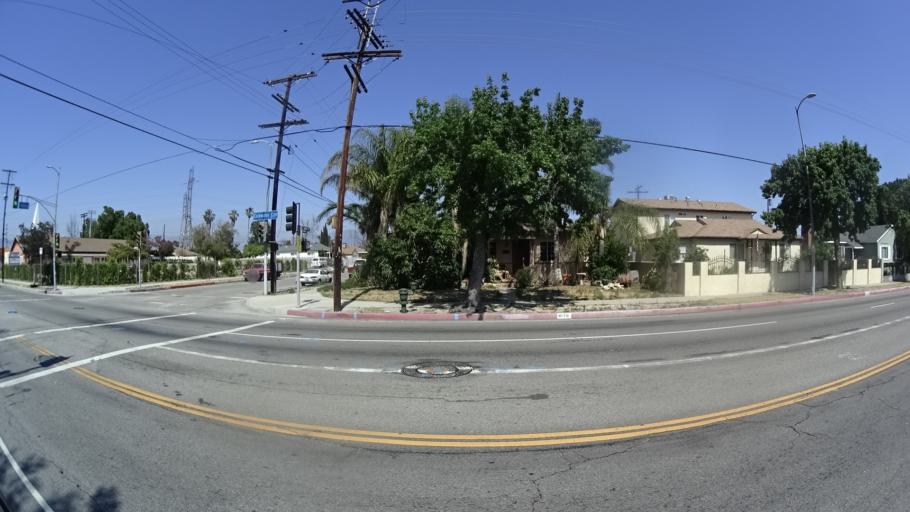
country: US
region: California
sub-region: Los Angeles County
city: Van Nuys
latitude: 34.2198
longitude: -118.4144
